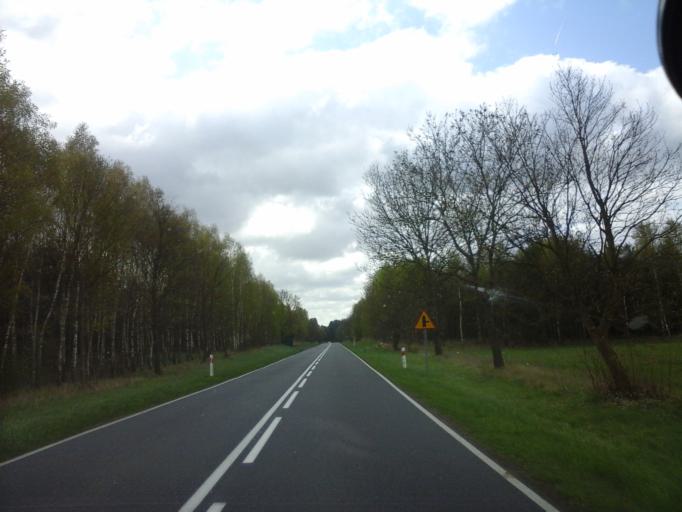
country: PL
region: West Pomeranian Voivodeship
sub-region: Powiat choszczenski
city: Bierzwnik
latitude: 53.0949
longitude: 15.6367
